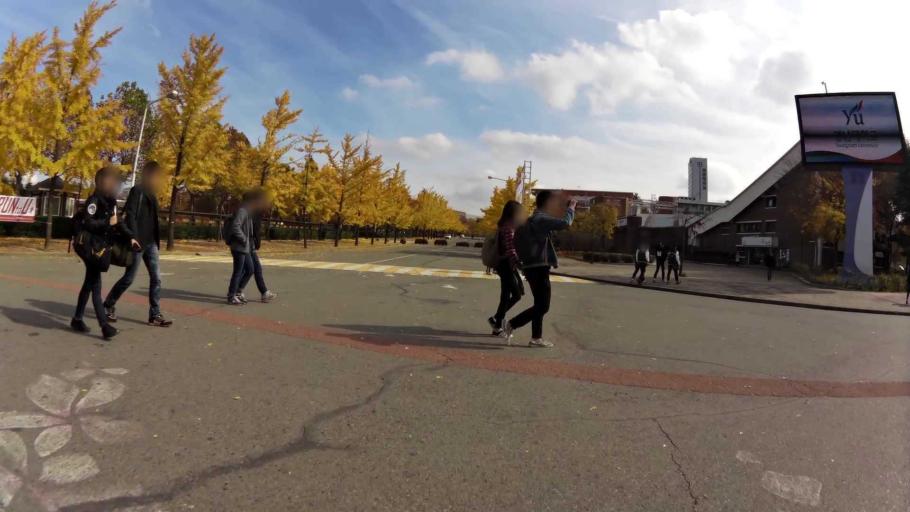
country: KR
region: Gyeongsangbuk-do
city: Gyeongsan-si
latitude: 35.8347
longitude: 128.7540
